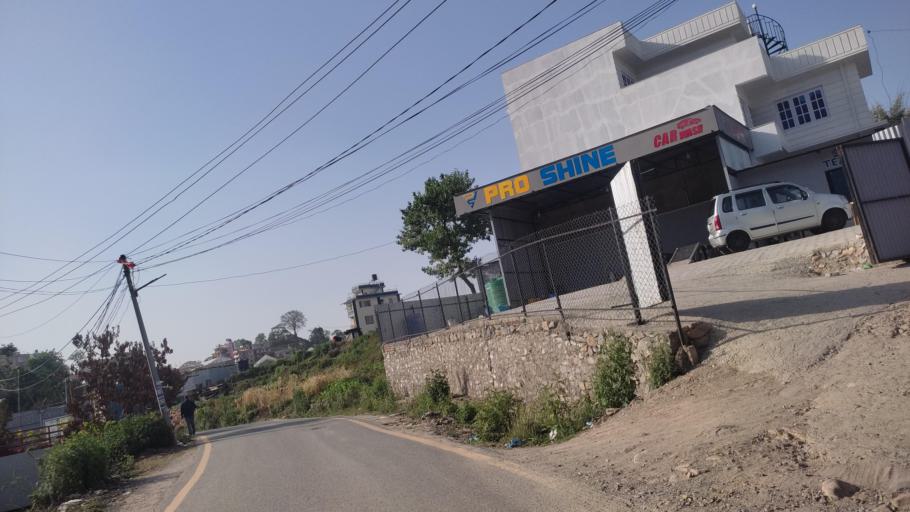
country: NP
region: Central Region
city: Kirtipur
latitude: 27.6495
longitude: 85.2792
